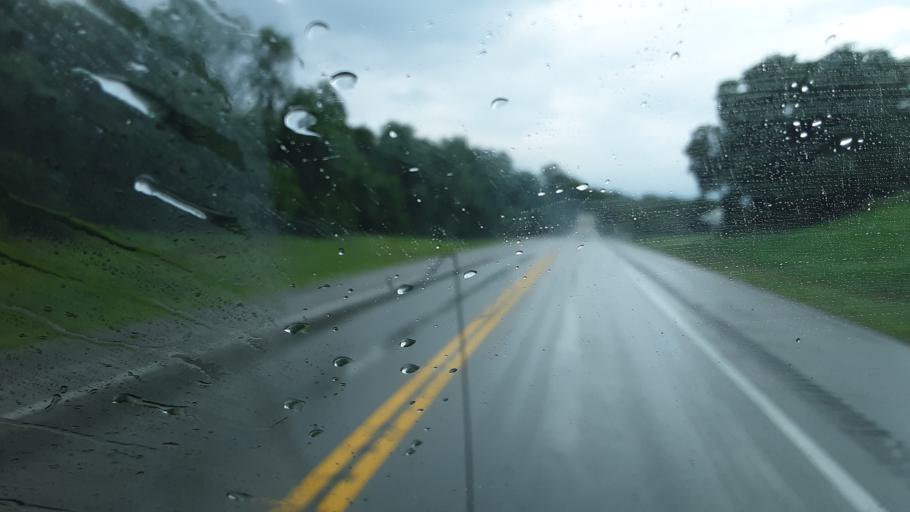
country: US
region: Kentucky
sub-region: Logan County
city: Russellville
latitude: 36.8194
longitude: -86.9287
